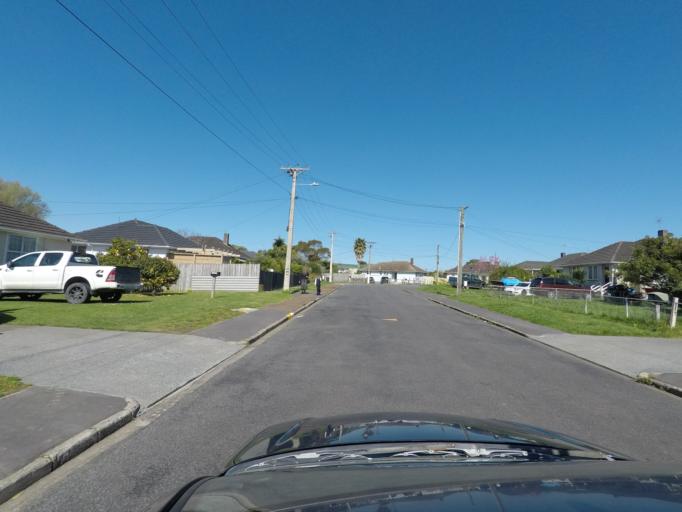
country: NZ
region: Auckland
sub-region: Auckland
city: Tamaki
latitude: -36.9259
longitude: 174.8596
